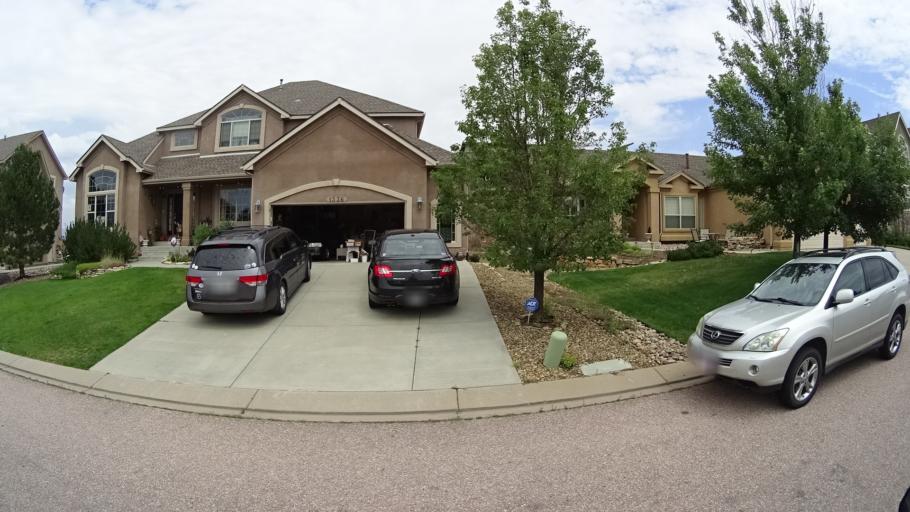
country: US
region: Colorado
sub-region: El Paso County
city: Gleneagle
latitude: 39.0161
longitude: -104.8024
